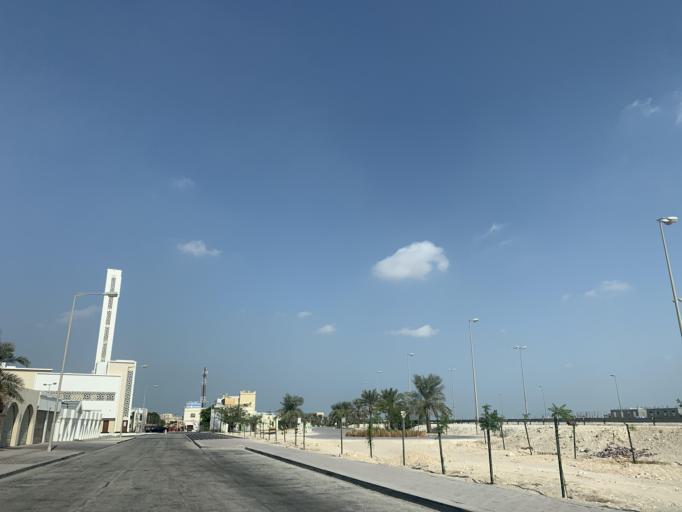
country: BH
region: Central Governorate
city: Madinat Hamad
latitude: 26.1242
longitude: 50.5057
